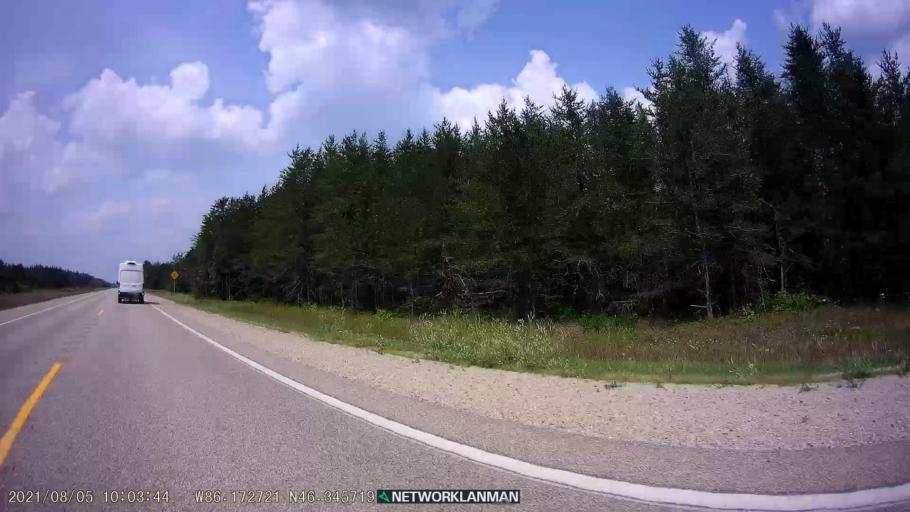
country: US
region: Michigan
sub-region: Schoolcraft County
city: Manistique
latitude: 46.3454
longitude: -86.1730
